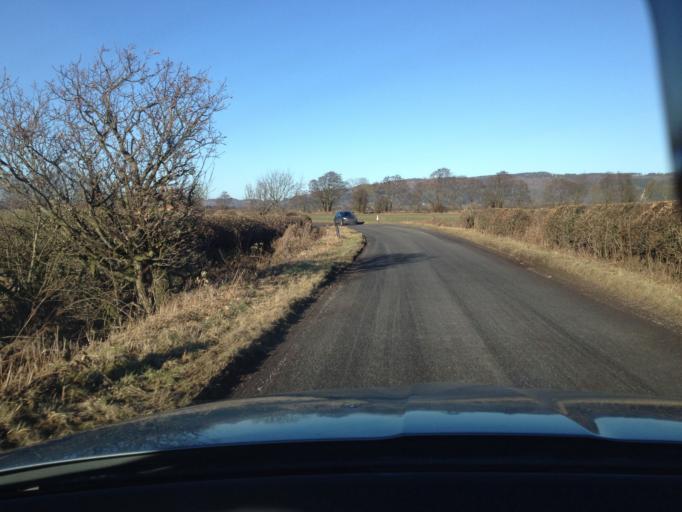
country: GB
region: Scotland
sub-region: Perth and Kinross
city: Bridge of Earn
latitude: 56.3281
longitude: -3.3793
